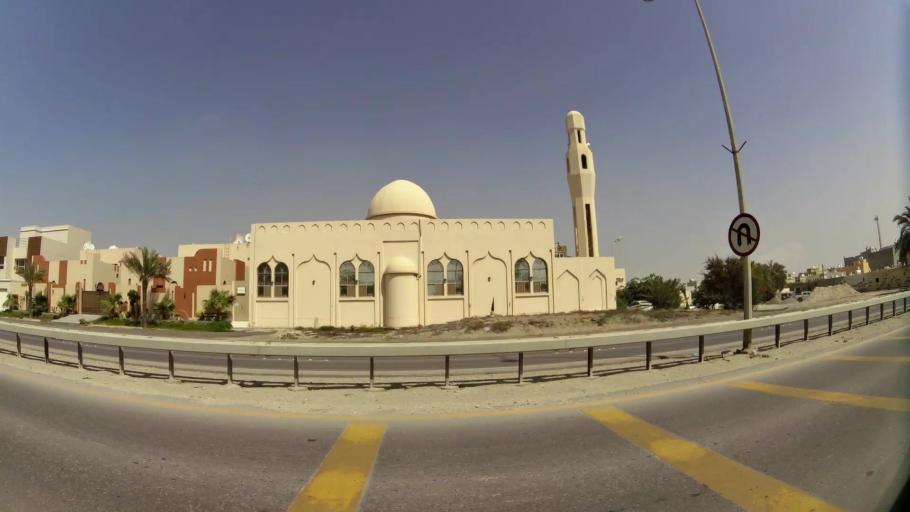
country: BH
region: Manama
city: Jidd Hafs
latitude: 26.1973
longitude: 50.4610
